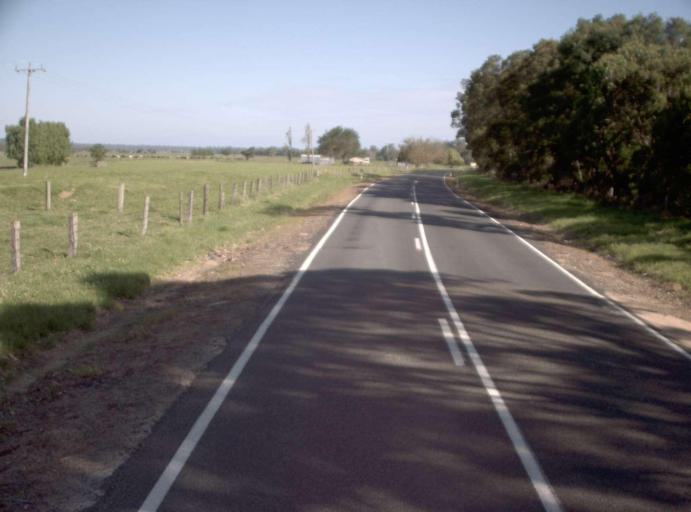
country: AU
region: Victoria
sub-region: East Gippsland
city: Lakes Entrance
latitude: -37.7438
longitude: 148.5143
